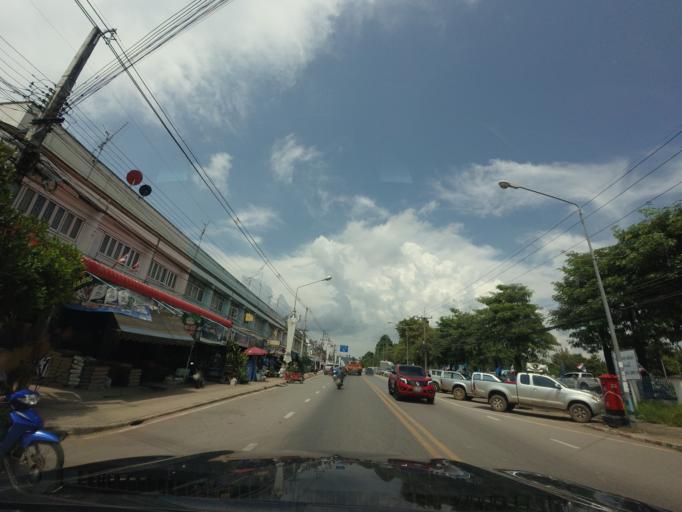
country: TH
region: Khon Kaen
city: Phu Wiang
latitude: 16.6532
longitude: 102.3770
